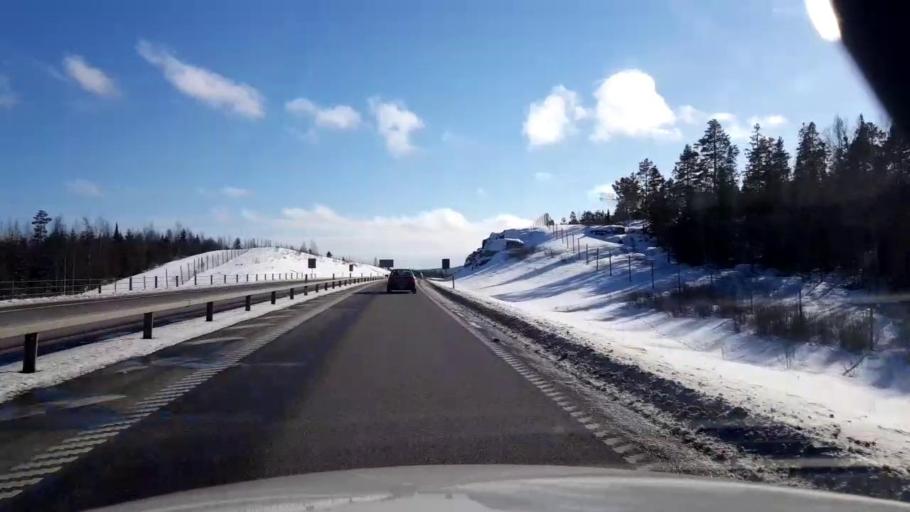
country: SE
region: Vaesternorrland
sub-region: Sundsvalls Kommun
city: Njurundabommen
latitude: 62.2602
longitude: 17.3642
